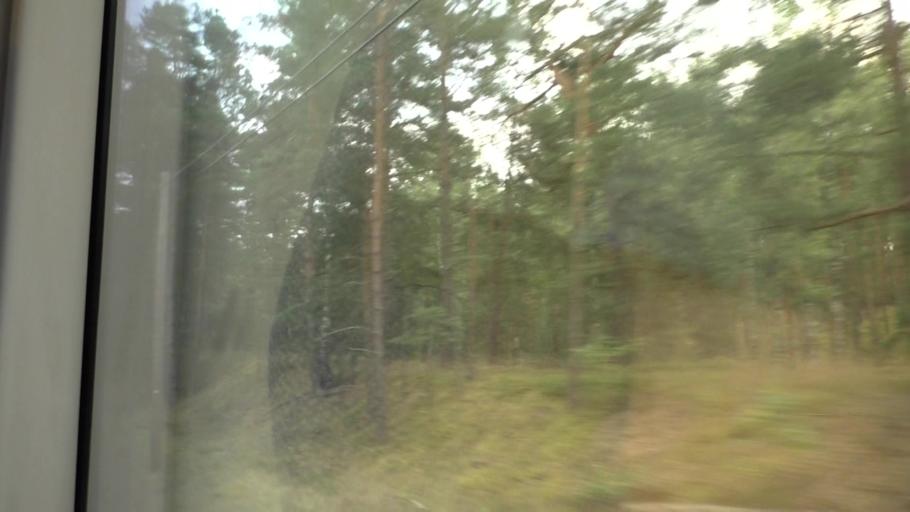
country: DE
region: Brandenburg
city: Wendisch Rietz
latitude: 52.2216
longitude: 13.9847
